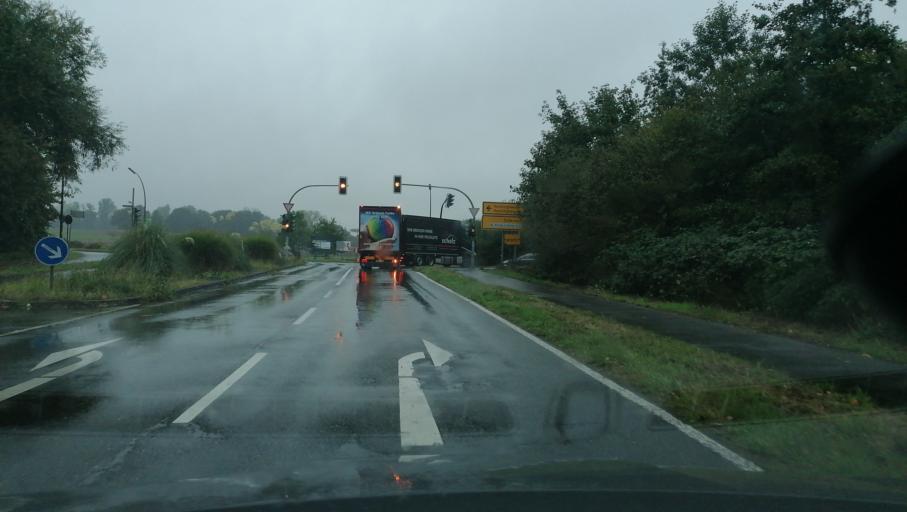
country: DE
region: North Rhine-Westphalia
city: Oer-Erkenschwick
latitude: 51.6049
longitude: 7.2438
